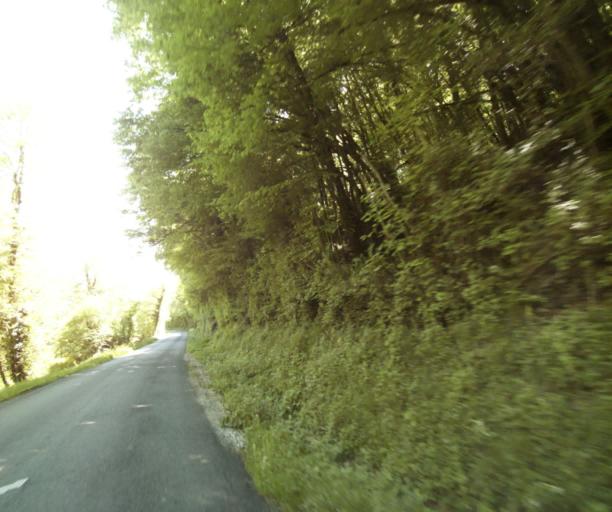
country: FR
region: Poitou-Charentes
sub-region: Departement de la Charente-Maritime
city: Chaniers
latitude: 45.7442
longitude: -0.5082
